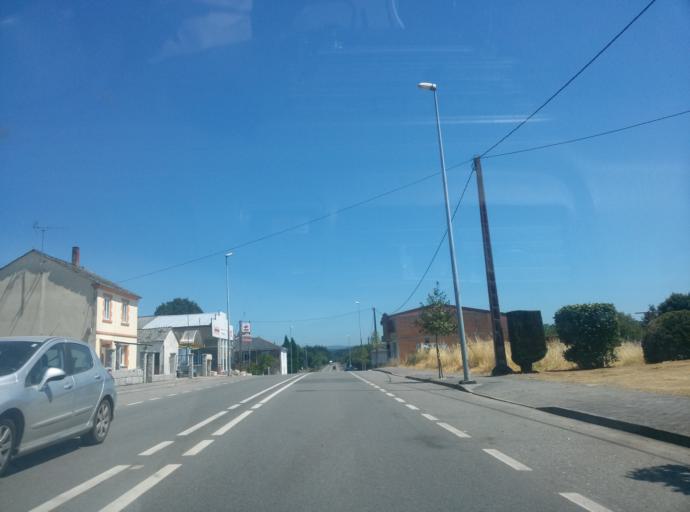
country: ES
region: Galicia
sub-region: Provincia de Lugo
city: Castro de Rei
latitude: 43.2514
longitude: -7.4255
